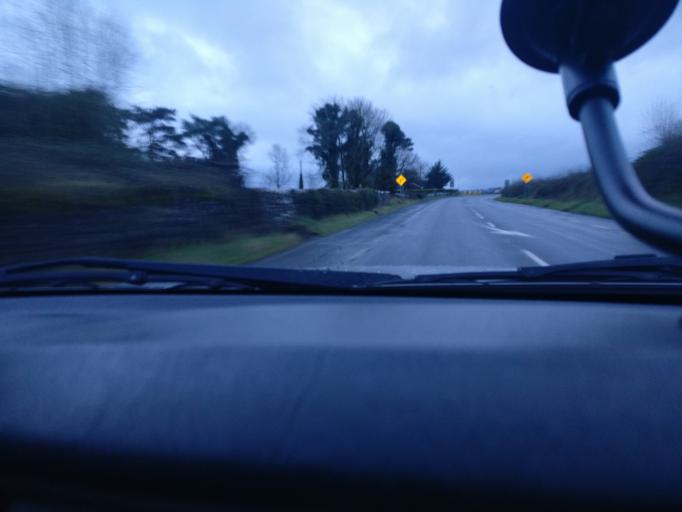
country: IE
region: Connaught
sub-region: County Galway
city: Loughrea
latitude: 53.2251
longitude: -8.4562
